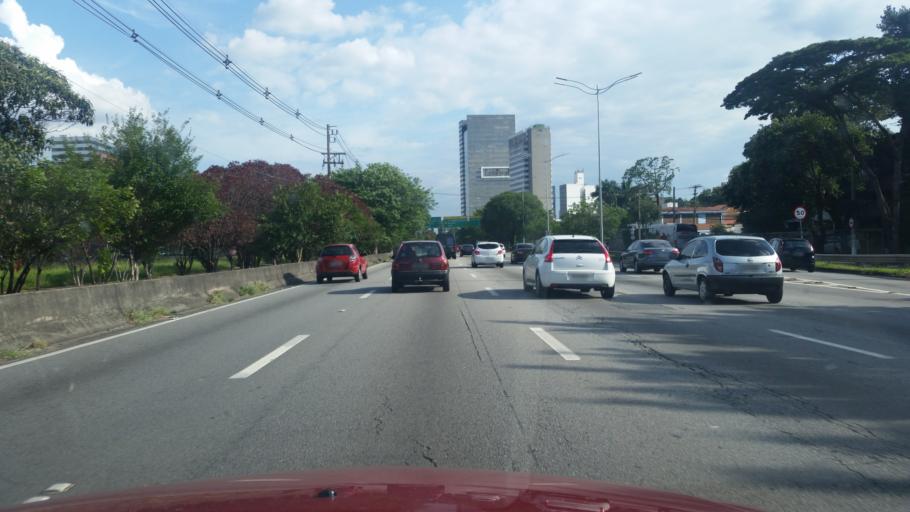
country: BR
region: Sao Paulo
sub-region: Sao Paulo
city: Sao Paulo
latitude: -23.5656
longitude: -46.7049
